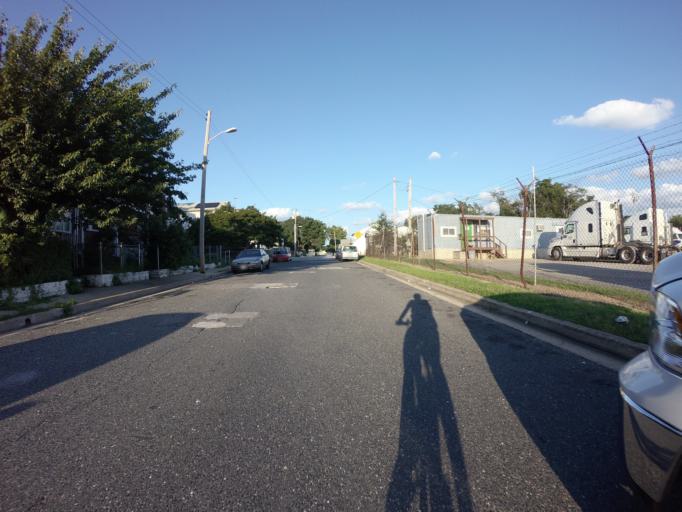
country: US
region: Maryland
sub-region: Baltimore County
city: Dundalk
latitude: 39.2575
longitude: -76.5302
